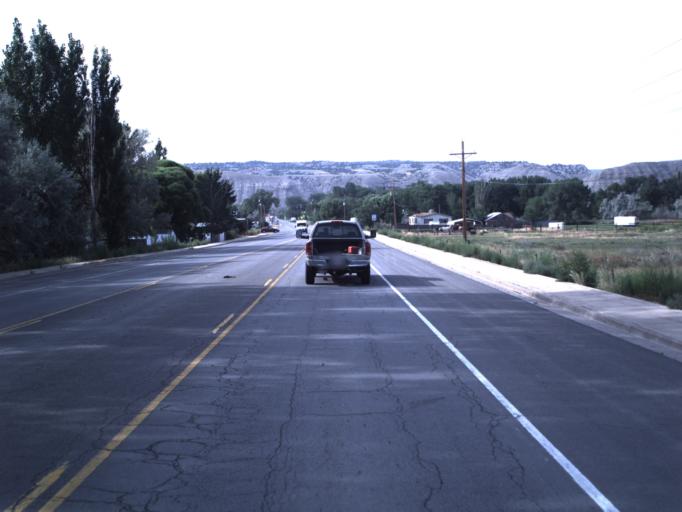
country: US
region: Utah
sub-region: Duchesne County
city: Duchesne
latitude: 40.1711
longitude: -110.4012
